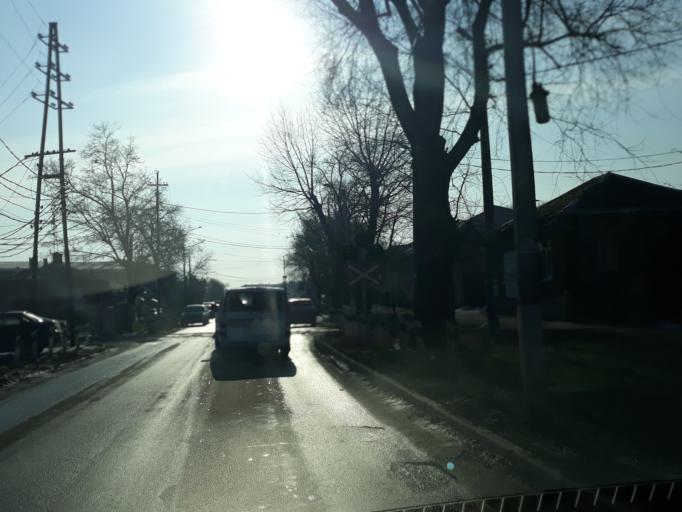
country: RU
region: Rostov
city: Taganrog
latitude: 47.2223
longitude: 38.9146
